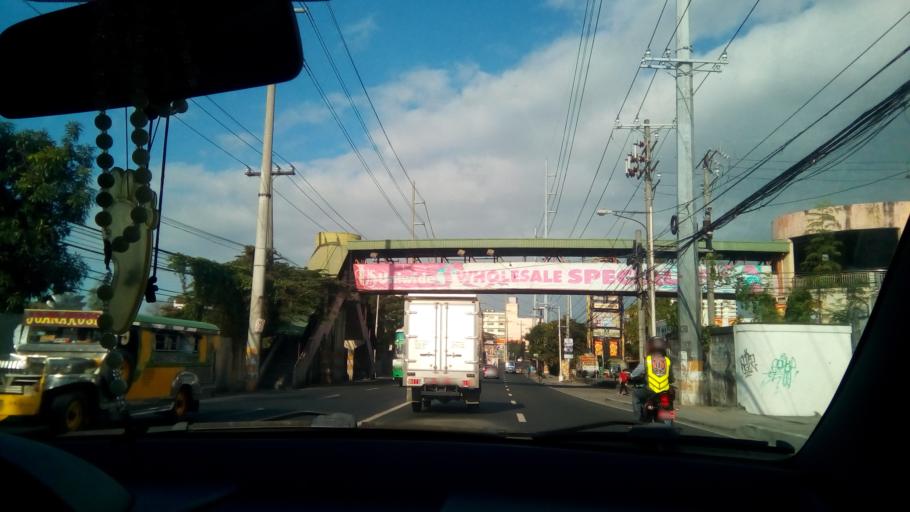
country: PH
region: Calabarzon
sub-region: Province of Rizal
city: Las Pinas
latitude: 14.4465
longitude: 120.9899
